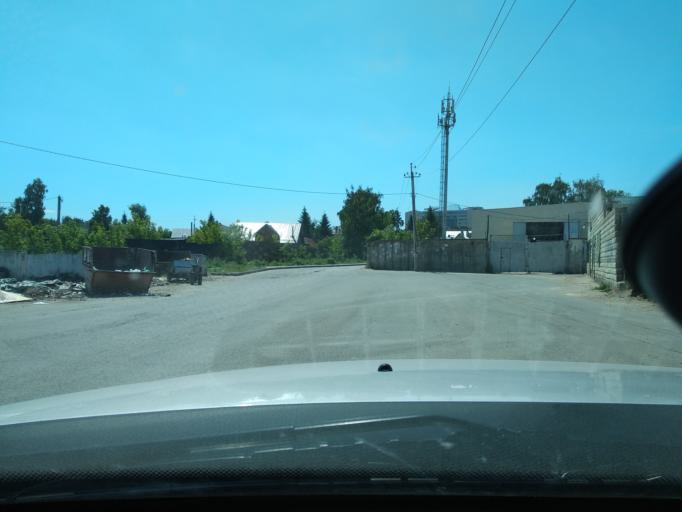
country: RU
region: Tatarstan
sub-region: Gorod Kazan'
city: Kazan
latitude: 55.8031
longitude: 49.2168
